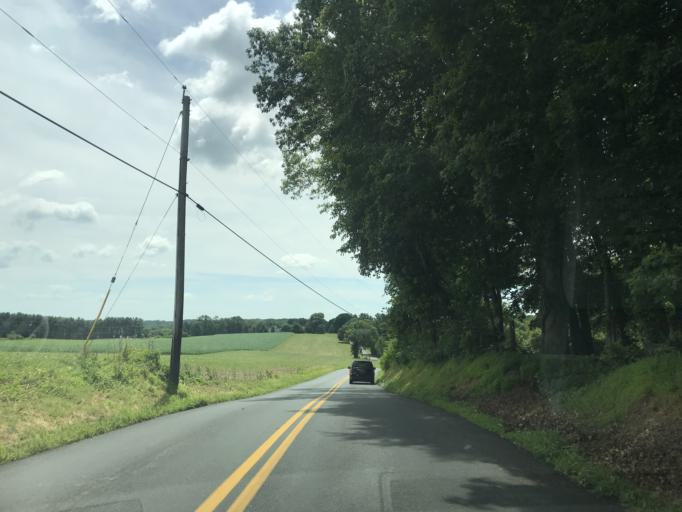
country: US
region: Maryland
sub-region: Carroll County
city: Hampstead
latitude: 39.6318
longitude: -76.8007
